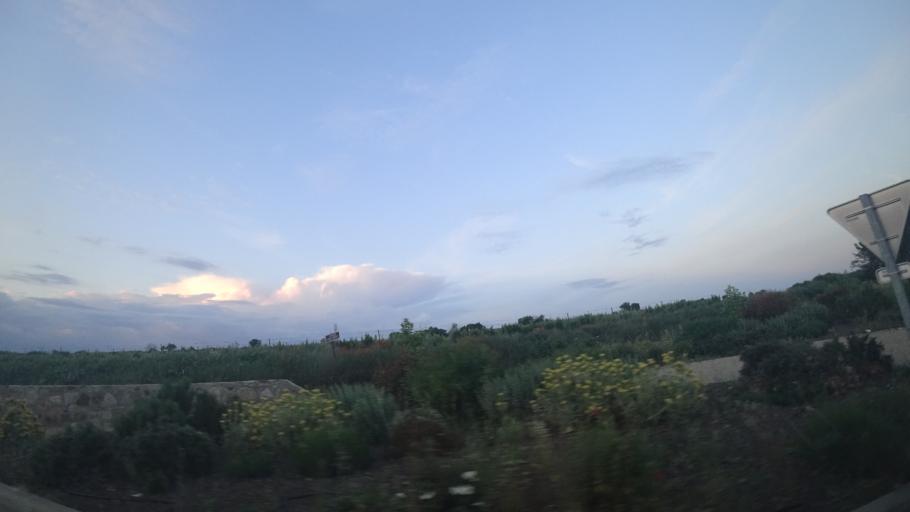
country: FR
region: Languedoc-Roussillon
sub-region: Departement de l'Herault
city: Capestang
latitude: 43.3251
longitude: 3.0560
